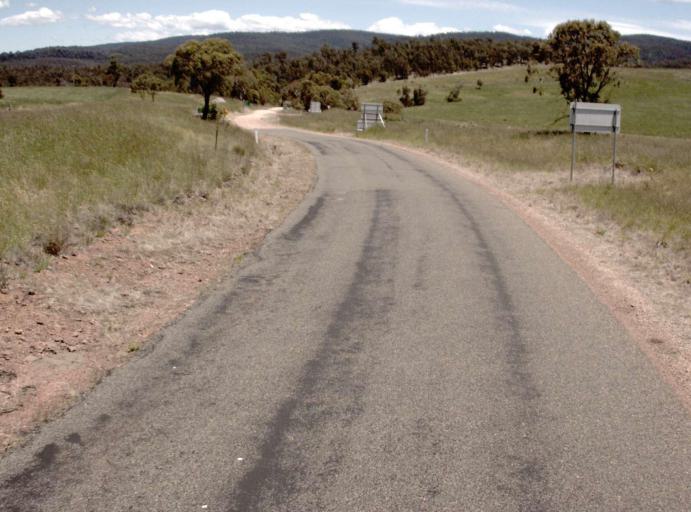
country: AU
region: New South Wales
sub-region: Snowy River
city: Jindabyne
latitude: -37.0994
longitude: 148.2534
